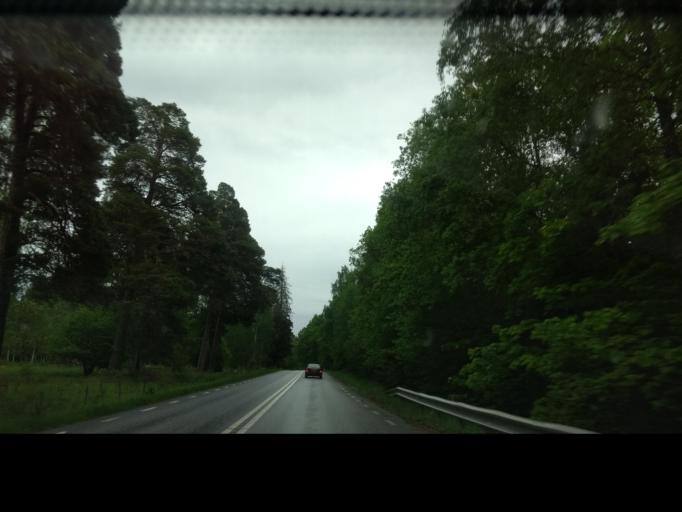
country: SE
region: Uppsala
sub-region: Uppsala Kommun
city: Saevja
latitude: 59.7606
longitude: 17.6456
